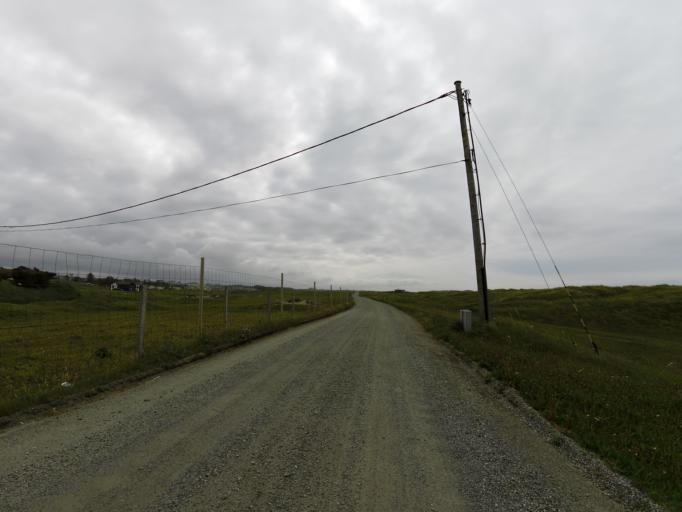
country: NO
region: Rogaland
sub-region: Klepp
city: Kleppe
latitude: 58.8043
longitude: 5.5514
